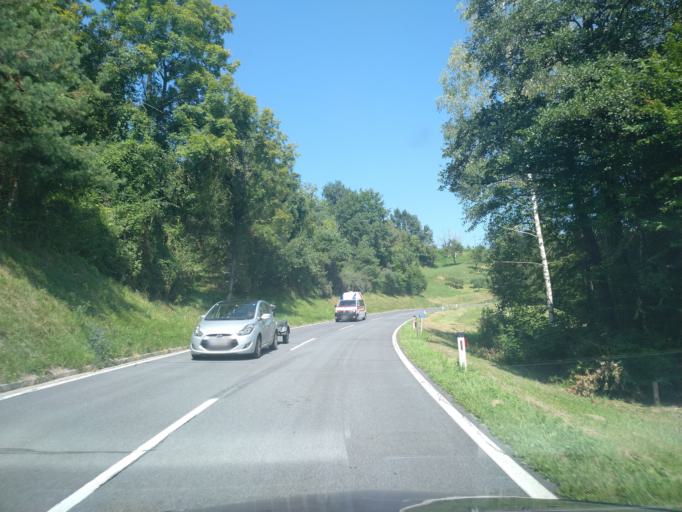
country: AT
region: Styria
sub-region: Politischer Bezirk Leibnitz
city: Leutschach
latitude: 46.6732
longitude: 15.4760
